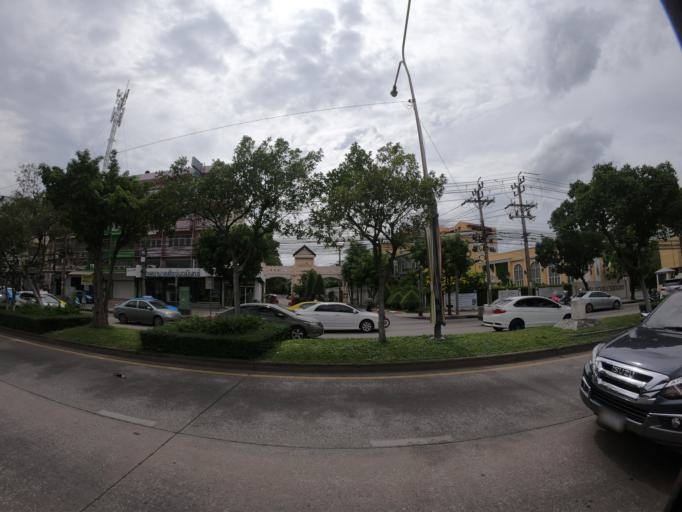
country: TH
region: Bangkok
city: Khan Na Yao
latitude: 13.8152
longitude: 100.6525
